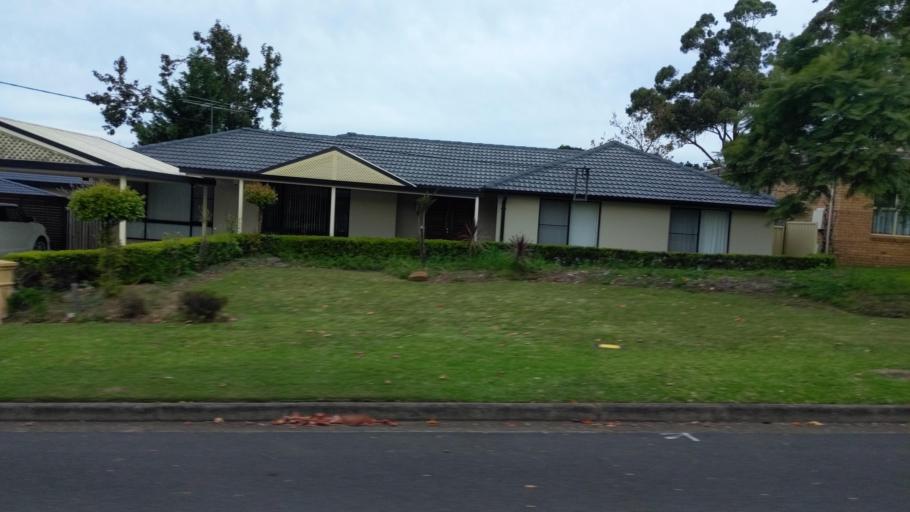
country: AU
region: New South Wales
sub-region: The Hills Shire
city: Baulkham Hills
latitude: -33.7484
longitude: 150.9654
